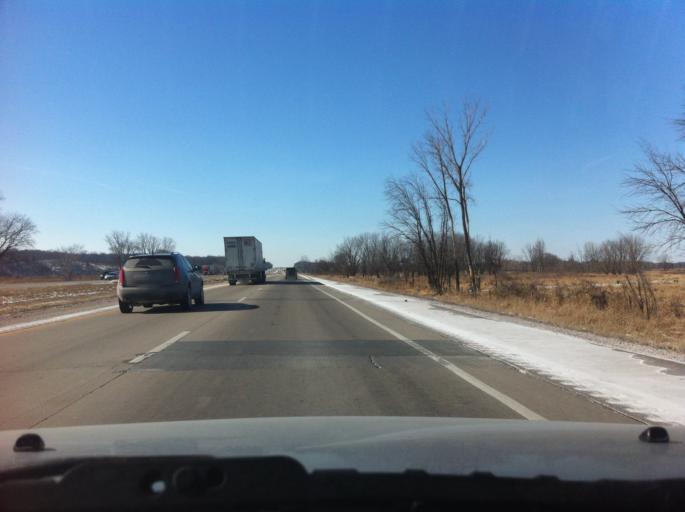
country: US
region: Wisconsin
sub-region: Columbia County
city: Portage
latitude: 43.5039
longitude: -89.5147
